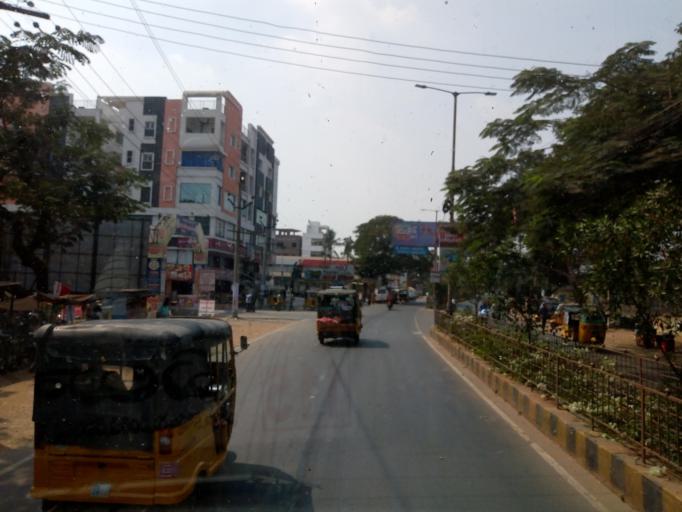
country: IN
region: Andhra Pradesh
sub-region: West Godavari
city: Eluru
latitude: 16.7082
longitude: 81.0895
